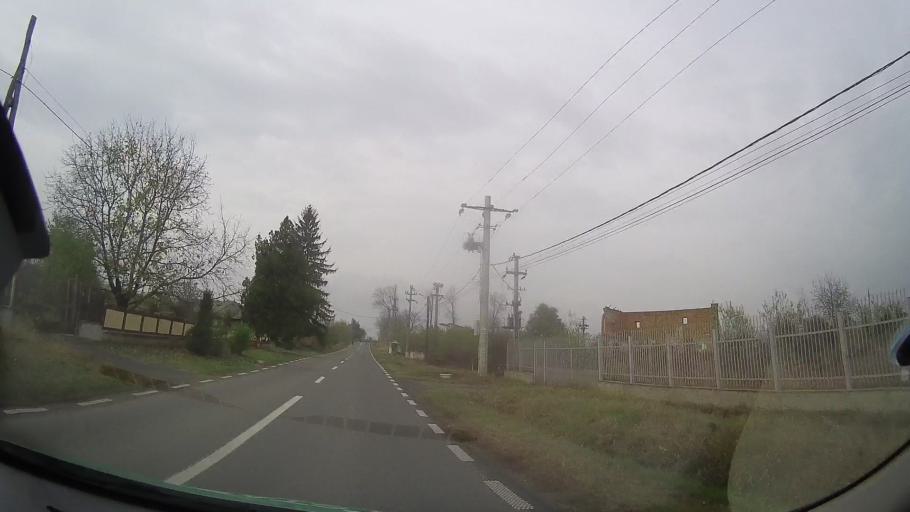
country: RO
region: Ilfov
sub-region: Comuna Gruiu
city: Lipia
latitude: 44.7160
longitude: 26.2514
